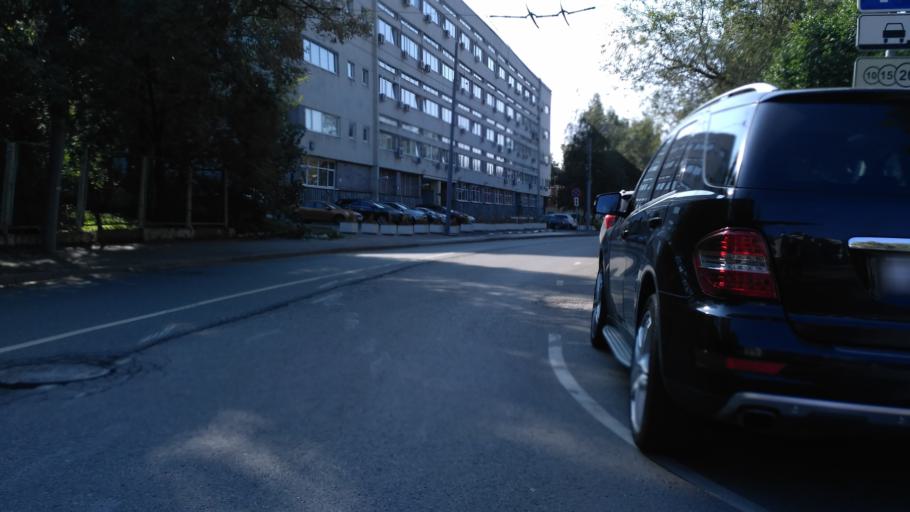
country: RU
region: Moscow
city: Lefortovo
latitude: 55.7655
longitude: 37.6749
